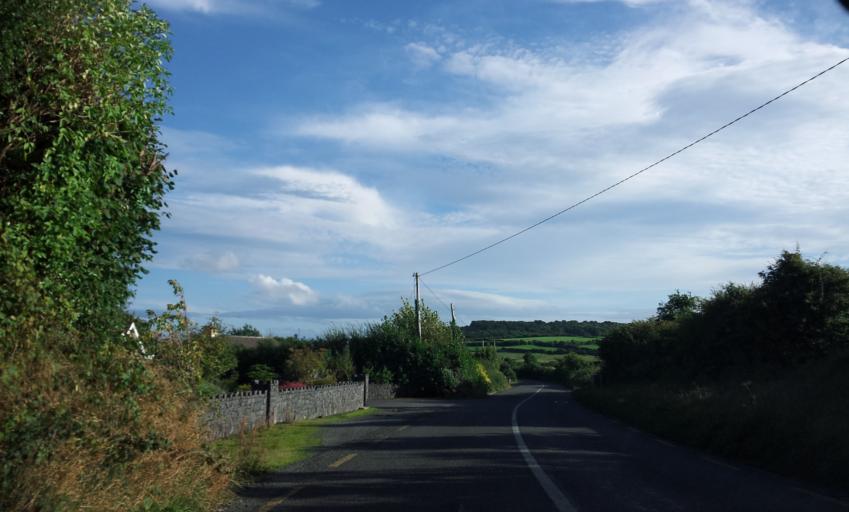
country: IE
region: Munster
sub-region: An Clar
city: Ennis
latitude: 52.9142
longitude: -9.0449
